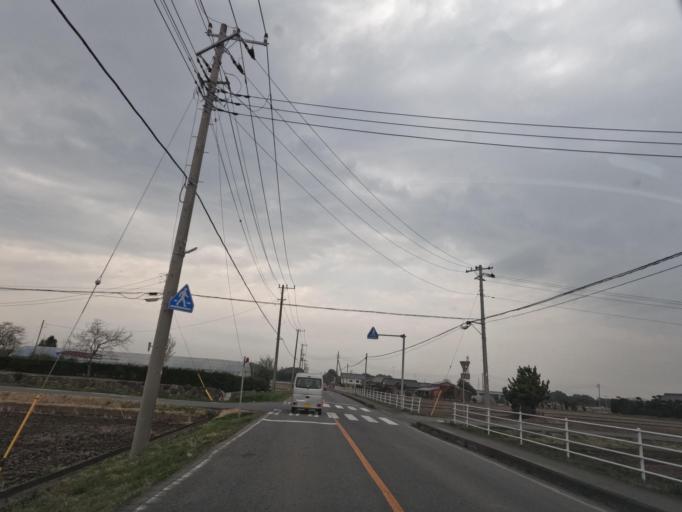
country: JP
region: Ibaraki
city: Moriya
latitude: 35.9800
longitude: 140.0210
